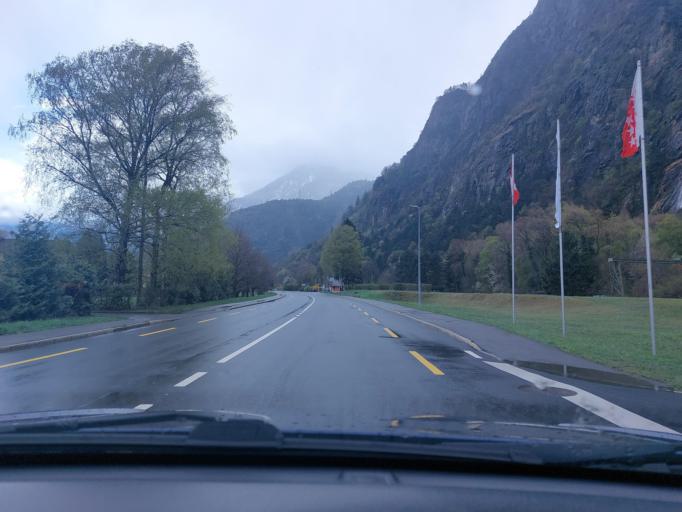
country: CH
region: Valais
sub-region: Saint-Maurice District
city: Vernayaz
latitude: 46.1463
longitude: 7.0300
